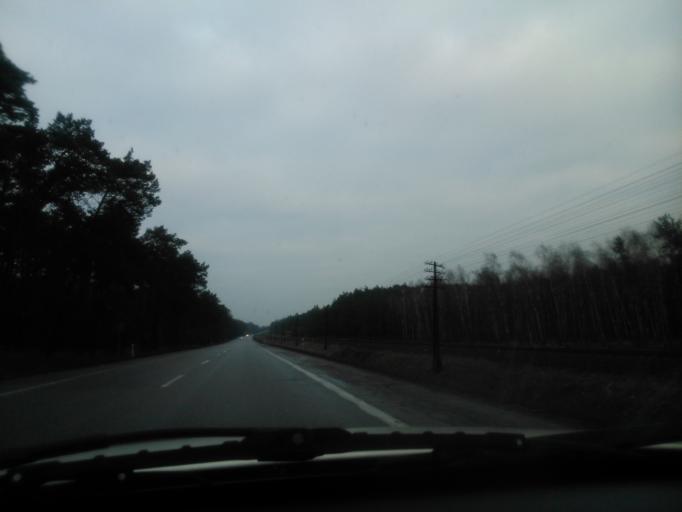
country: PL
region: Kujawsko-Pomorskie
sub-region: Powiat torunski
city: Lysomice
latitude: 53.0619
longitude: 18.6176
